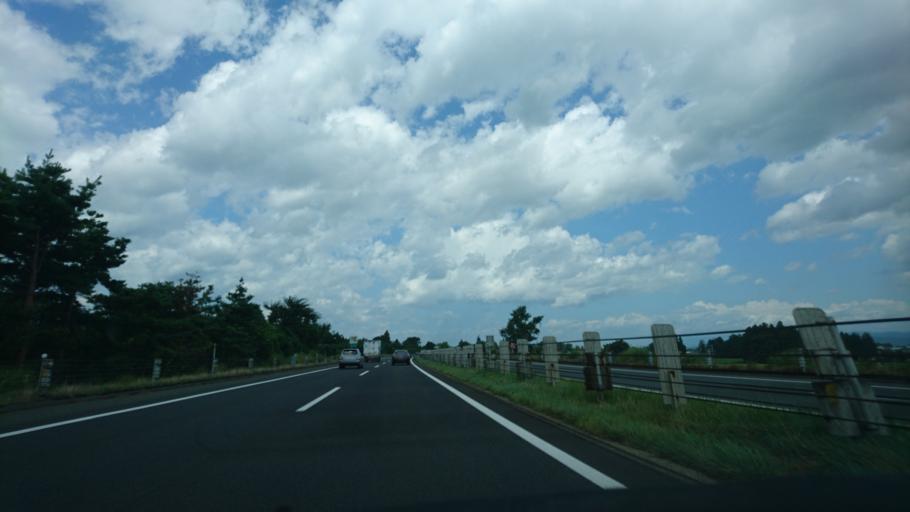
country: JP
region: Iwate
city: Morioka-shi
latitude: 39.5867
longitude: 141.1177
